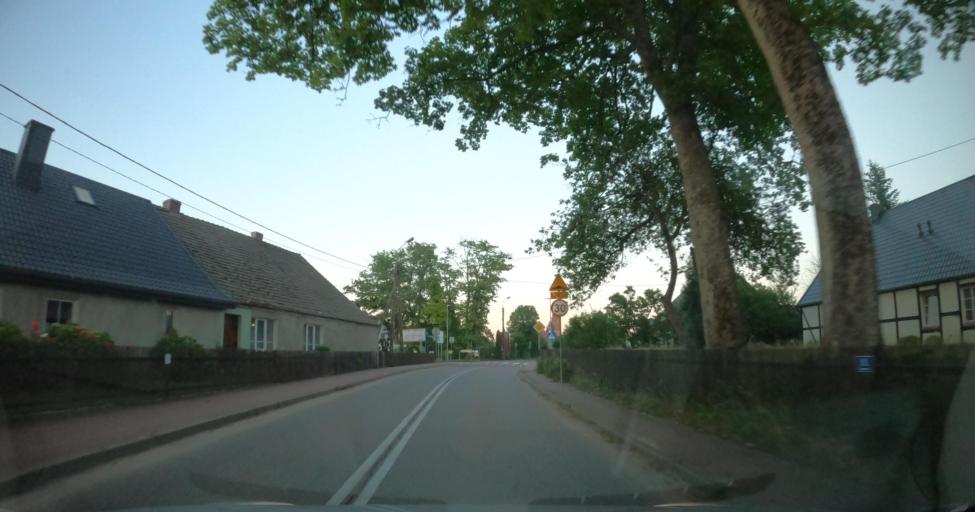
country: PL
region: Pomeranian Voivodeship
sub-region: Powiat wejherowski
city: Linia
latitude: 54.4566
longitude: 18.0204
